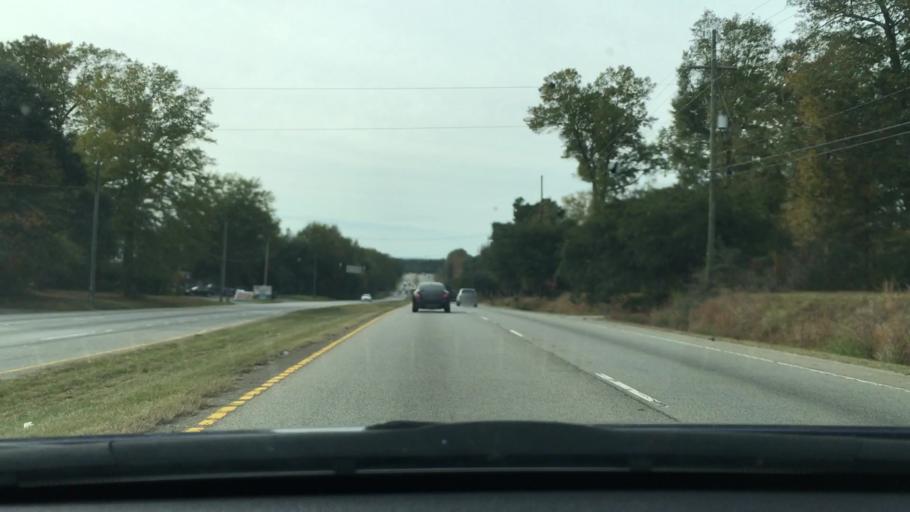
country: US
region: South Carolina
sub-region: Richland County
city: Hopkins
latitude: 33.9517
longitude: -80.8432
